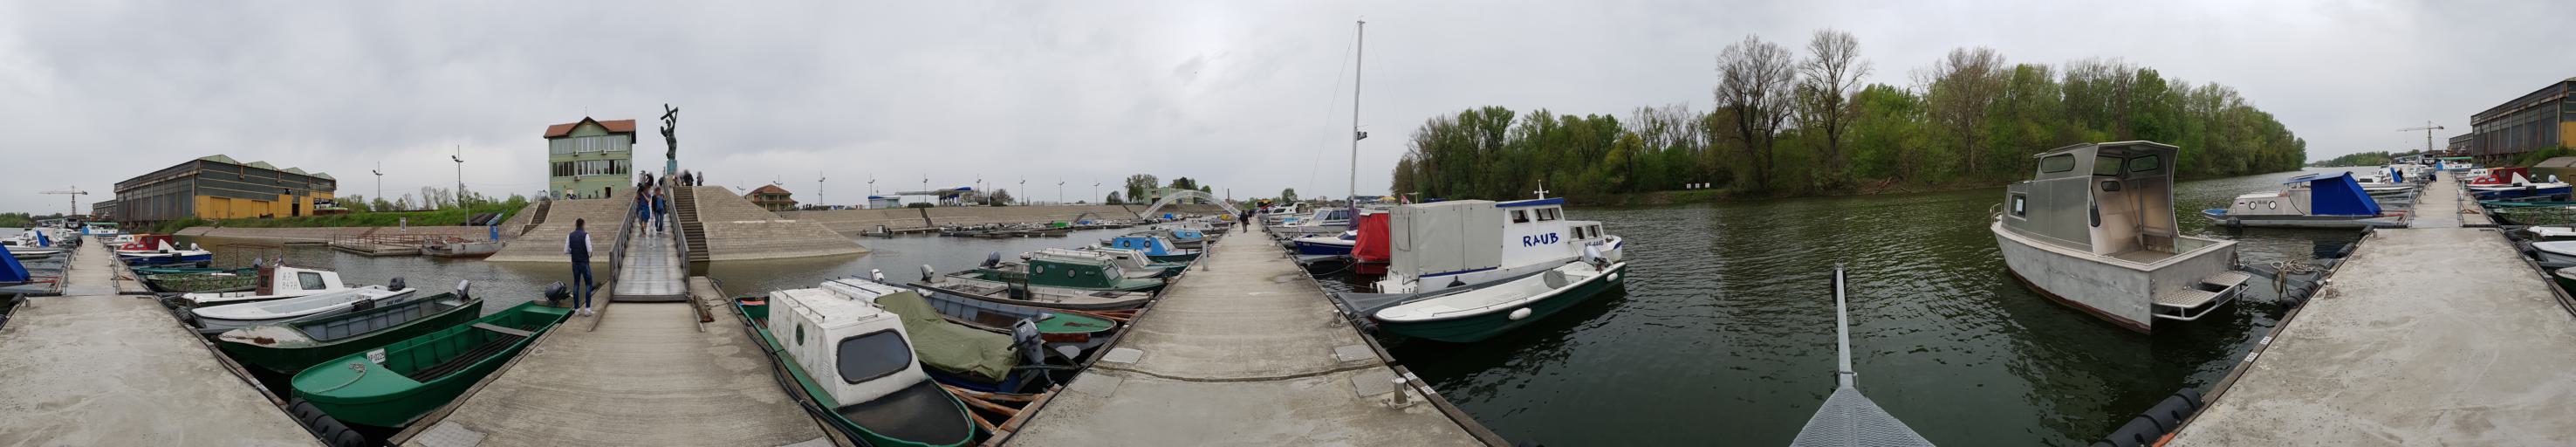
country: RS
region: Autonomna Pokrajina Vojvodina
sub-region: Zapadnobacki Okrug
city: Apatin
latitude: 45.6777
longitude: 18.9672
